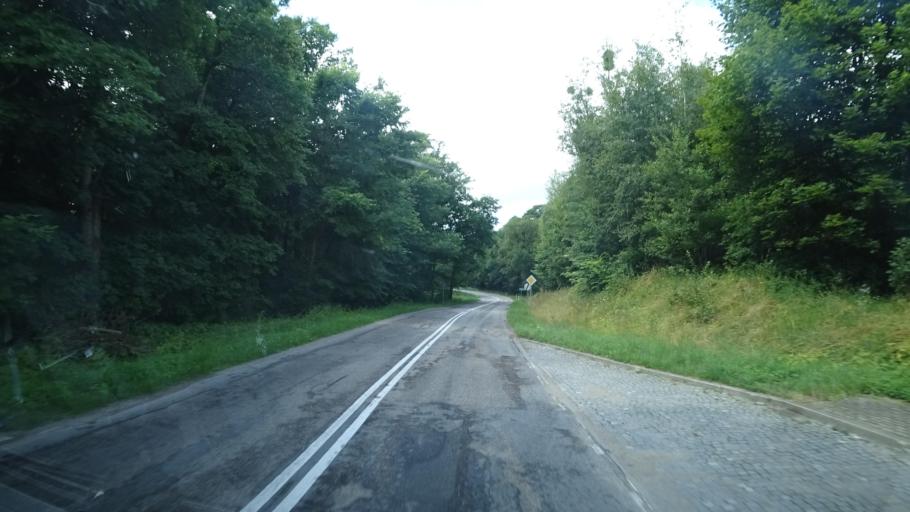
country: PL
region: Warmian-Masurian Voivodeship
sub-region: Powiat goldapski
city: Goldap
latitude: 54.2108
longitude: 22.2089
